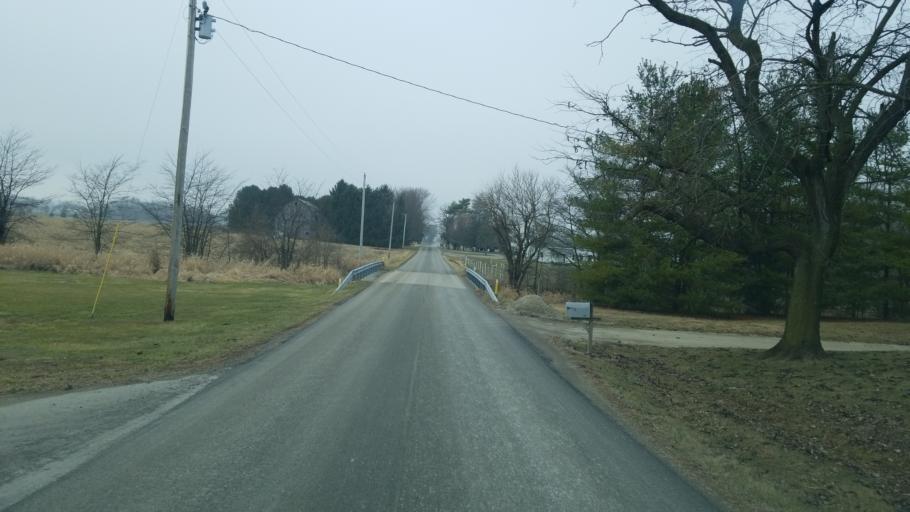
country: US
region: Indiana
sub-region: Adams County
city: Berne
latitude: 40.6878
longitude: -84.8922
